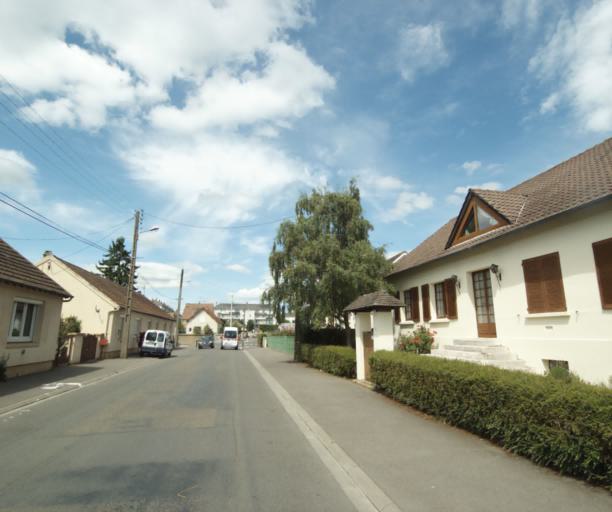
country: FR
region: Centre
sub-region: Departement d'Eure-et-Loir
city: Luce
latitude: 48.4354
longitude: 1.4589
